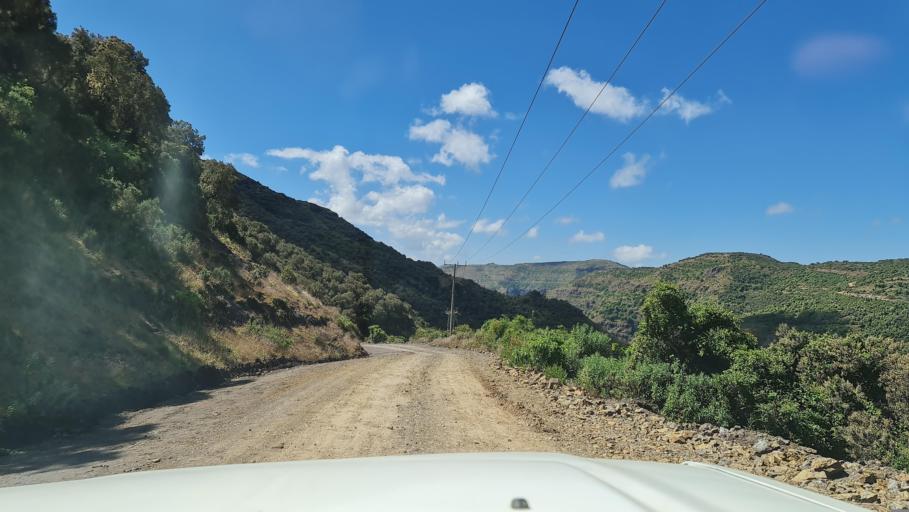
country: ET
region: Amhara
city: Debark'
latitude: 13.2330
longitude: 38.0668
